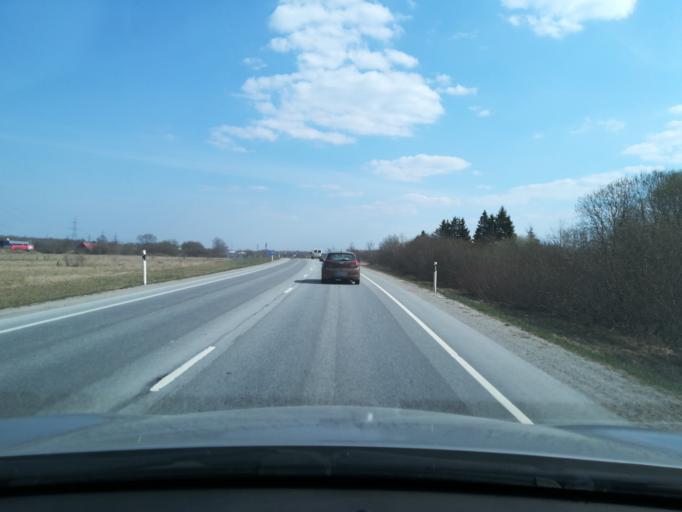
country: EE
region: Harju
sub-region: Harku vald
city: Tabasalu
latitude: 59.3907
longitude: 24.5724
